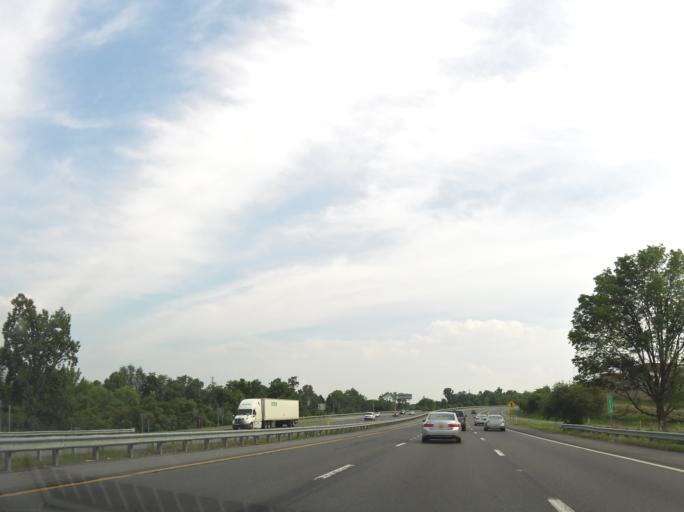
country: US
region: West Virginia
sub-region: Berkeley County
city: Martinsburg
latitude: 39.4430
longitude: -77.9893
